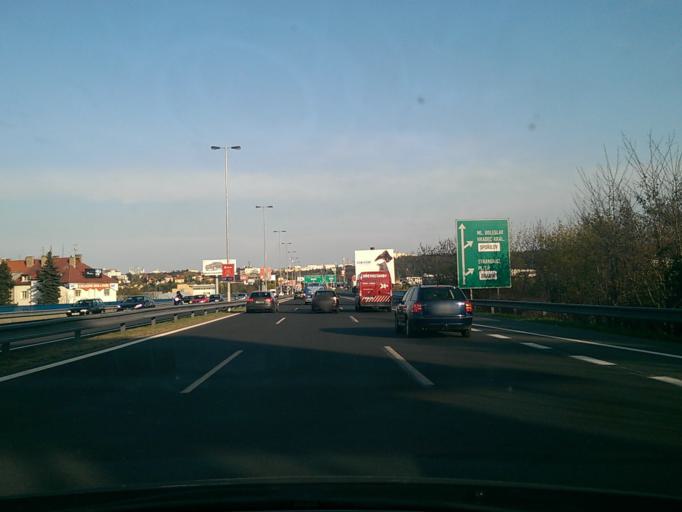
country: CZ
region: Praha
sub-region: Praha 4
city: Hodkovicky
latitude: 50.0436
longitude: 14.4609
